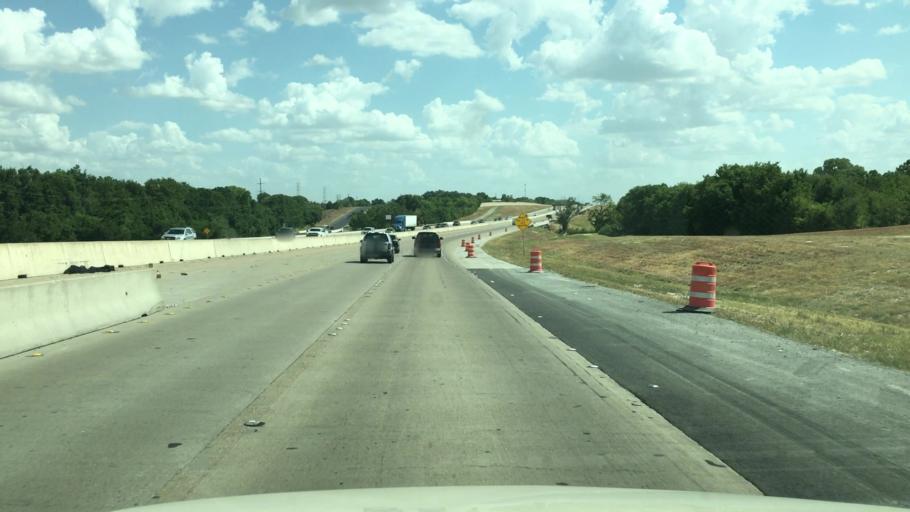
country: US
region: Texas
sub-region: Ellis County
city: Waxahachie
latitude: 32.3493
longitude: -96.8547
